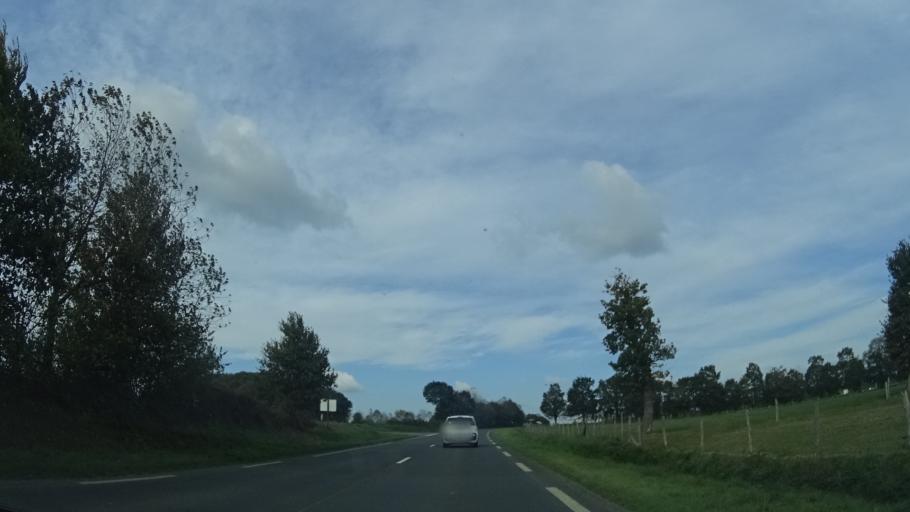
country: FR
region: Brittany
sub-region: Departement d'Ille-et-Vilaine
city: Hede-Bazouges
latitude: 48.3257
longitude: -1.7917
